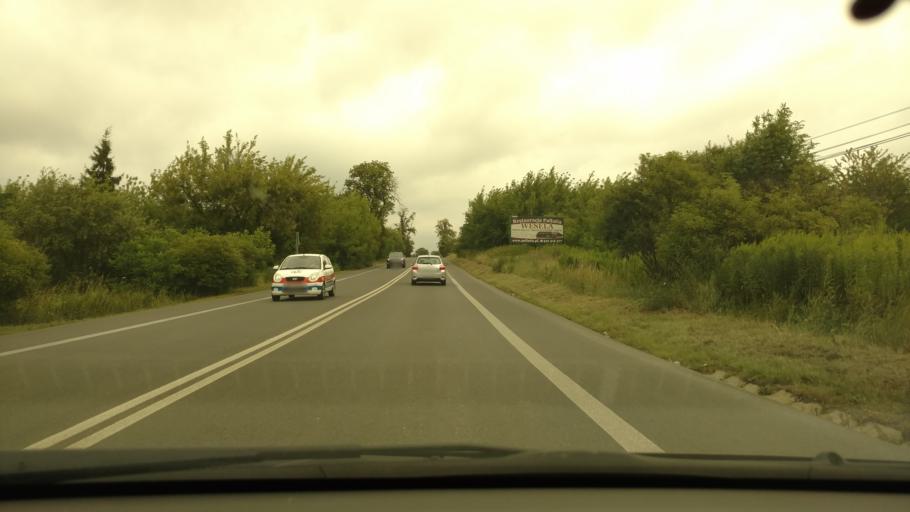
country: PL
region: Lesser Poland Voivodeship
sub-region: Powiat krakowski
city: Zielonki
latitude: 50.1019
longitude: 19.9635
